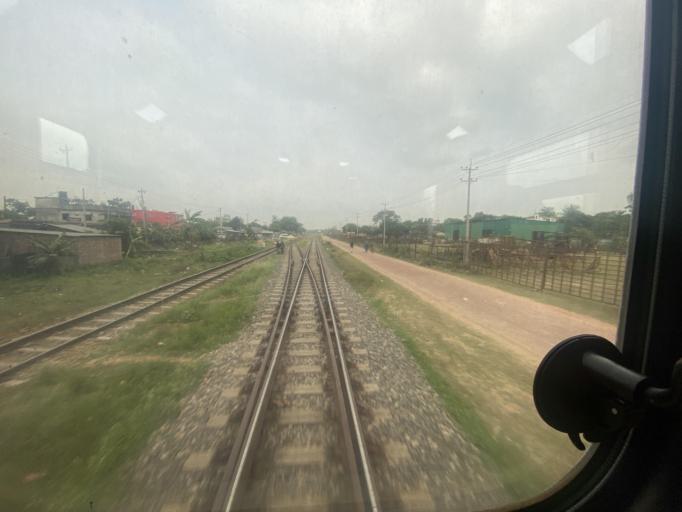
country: BD
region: Dhaka
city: Tungi
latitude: 23.9364
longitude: 90.4816
